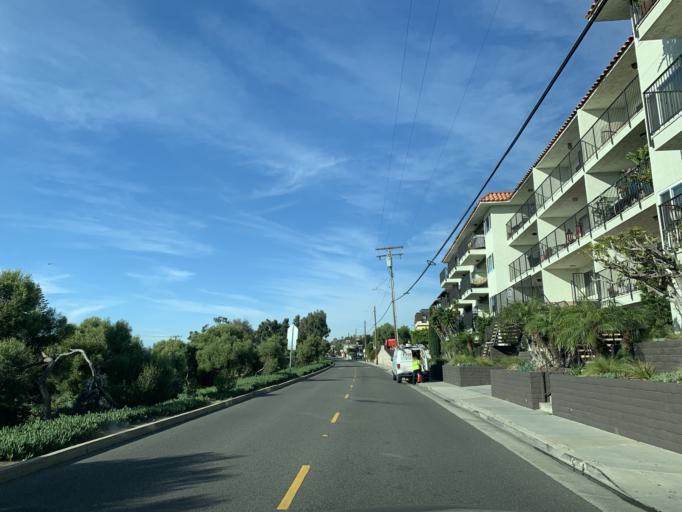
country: US
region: California
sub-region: Los Angeles County
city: Hermosa Beach
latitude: 33.8670
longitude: -118.3958
